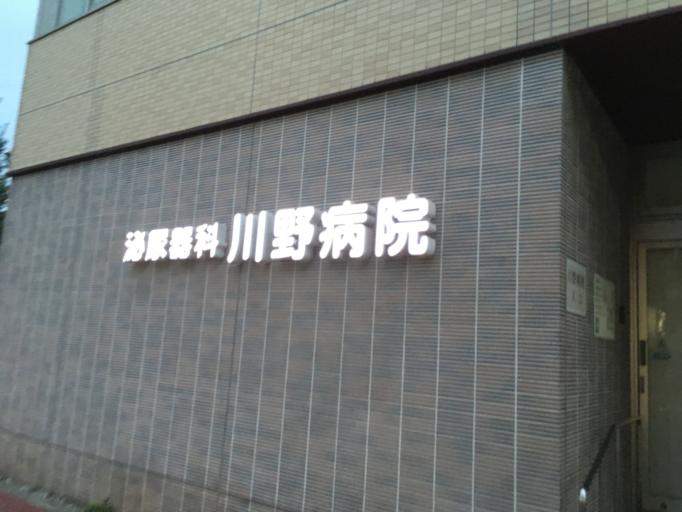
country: JP
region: Kumamoto
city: Kumamoto
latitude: 32.7952
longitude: 130.7255
